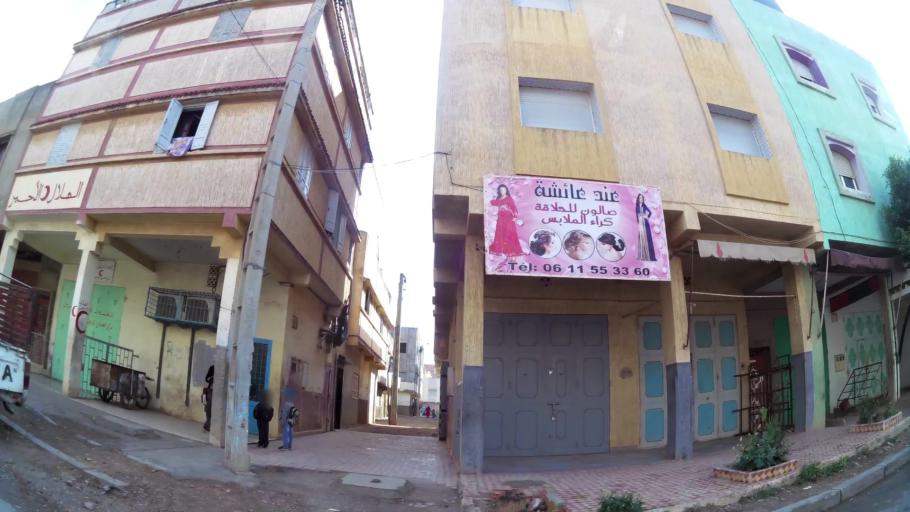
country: MA
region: Rabat-Sale-Zemmour-Zaer
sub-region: Khemisset
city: Tiflet
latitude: 33.8970
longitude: -6.3185
